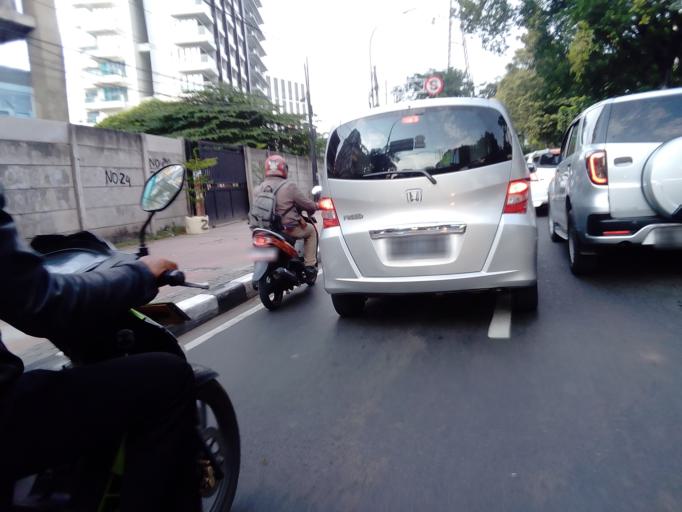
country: ID
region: Jakarta Raya
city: Jakarta
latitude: -6.1811
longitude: 106.8385
